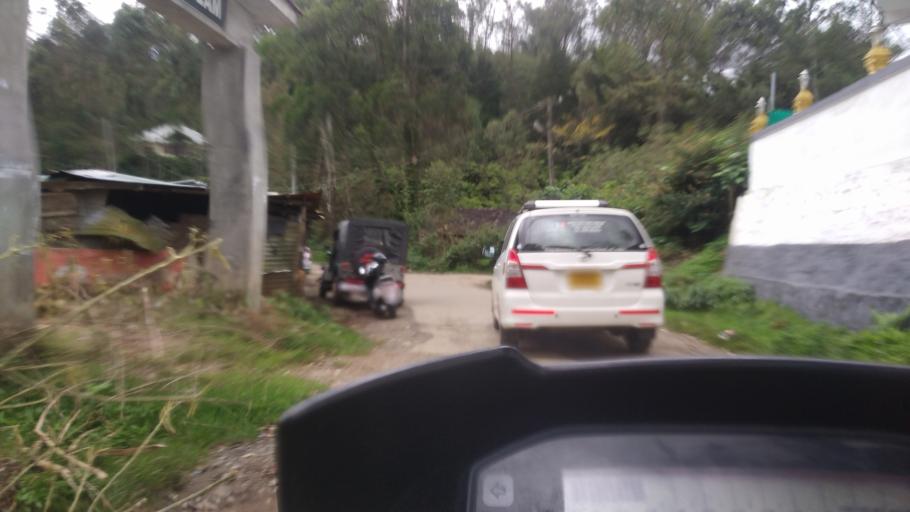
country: IN
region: Kerala
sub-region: Idukki
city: Munnar
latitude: 10.0643
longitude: 77.1076
